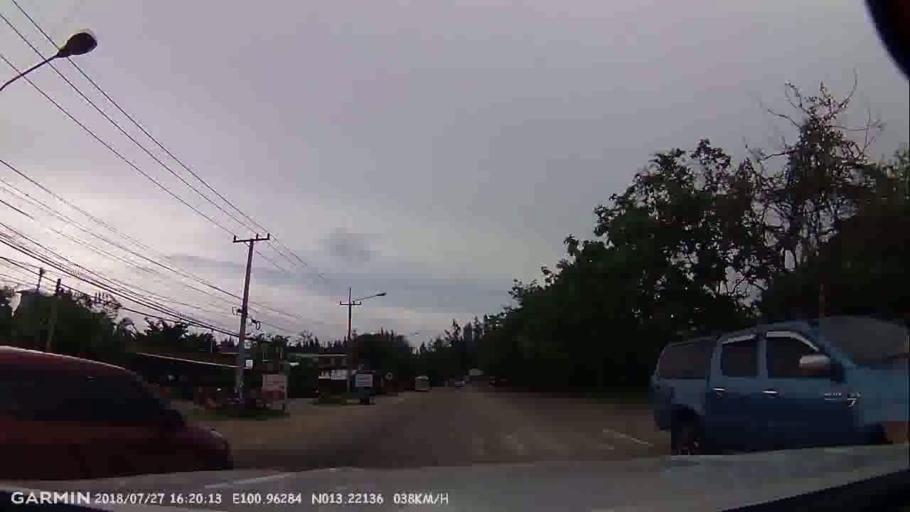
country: TH
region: Chon Buri
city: Si Racha
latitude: 13.2214
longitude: 100.9628
